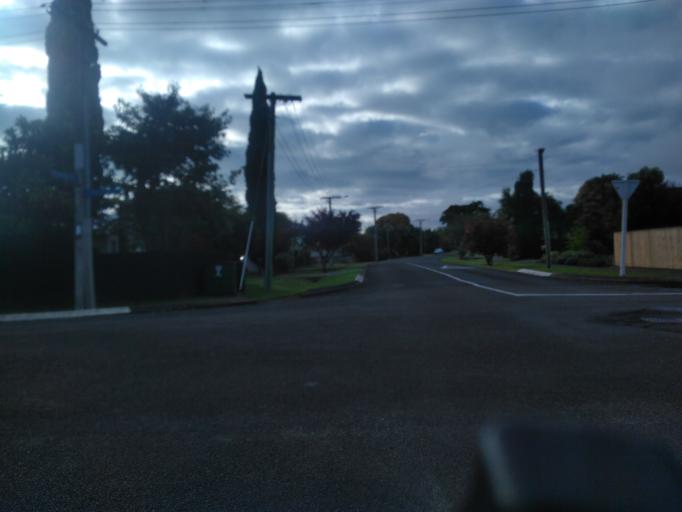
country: NZ
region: Gisborne
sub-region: Gisborne District
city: Gisborne
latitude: -38.6573
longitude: 178.0293
